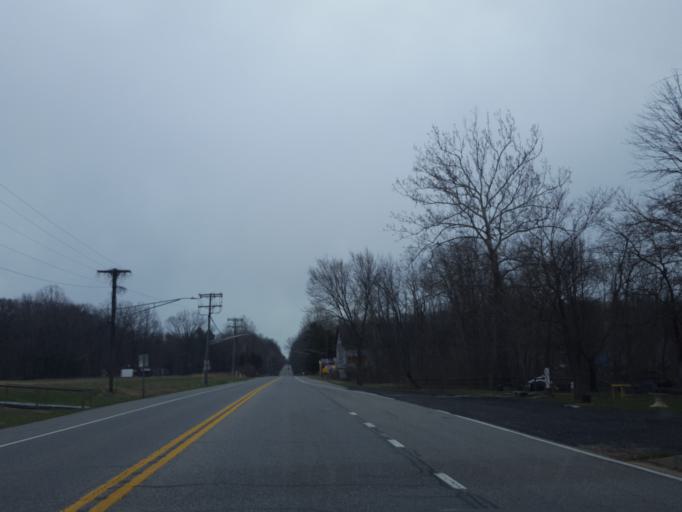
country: US
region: Maryland
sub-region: Calvert County
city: Owings
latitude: 38.7173
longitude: -76.6011
